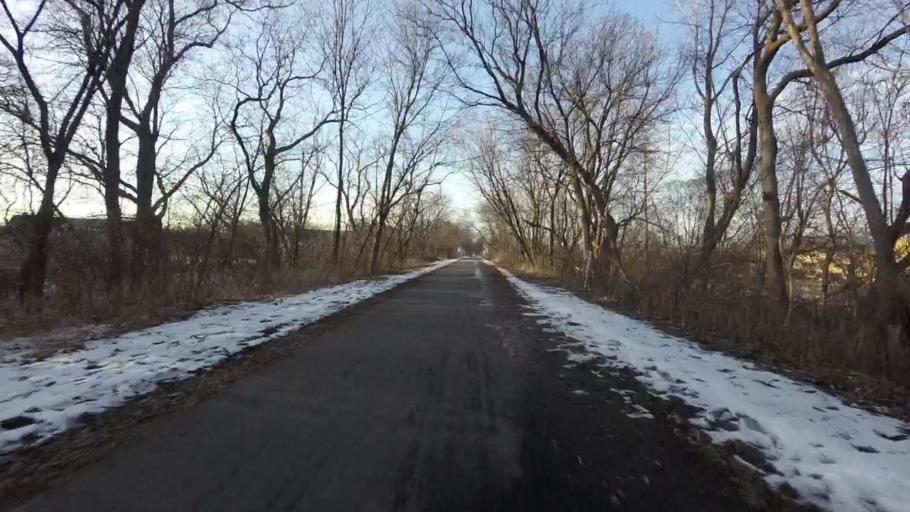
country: US
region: Wisconsin
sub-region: Milwaukee County
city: Whitefish Bay
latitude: 43.1079
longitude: -87.9150
